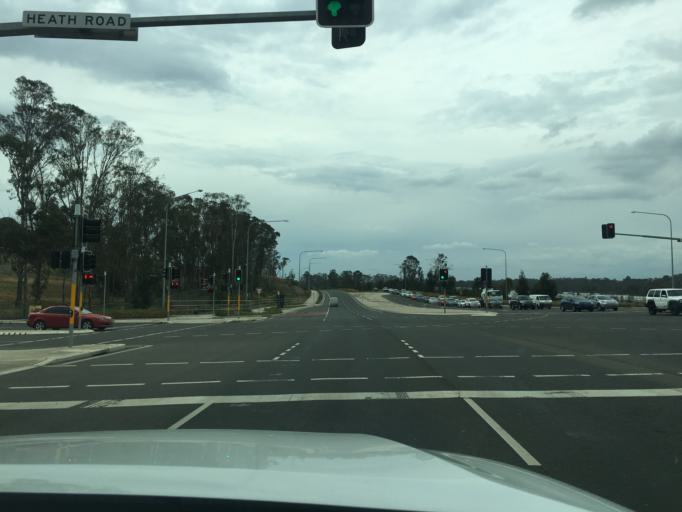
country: AU
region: New South Wales
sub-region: Campbelltown Municipality
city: Denham Court
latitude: -33.9762
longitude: 150.8092
